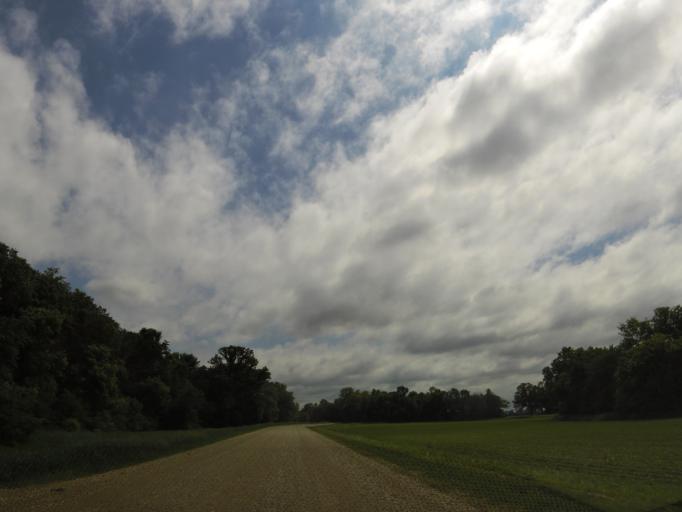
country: US
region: North Dakota
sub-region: Walsh County
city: Grafton
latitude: 48.4227
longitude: -97.4919
